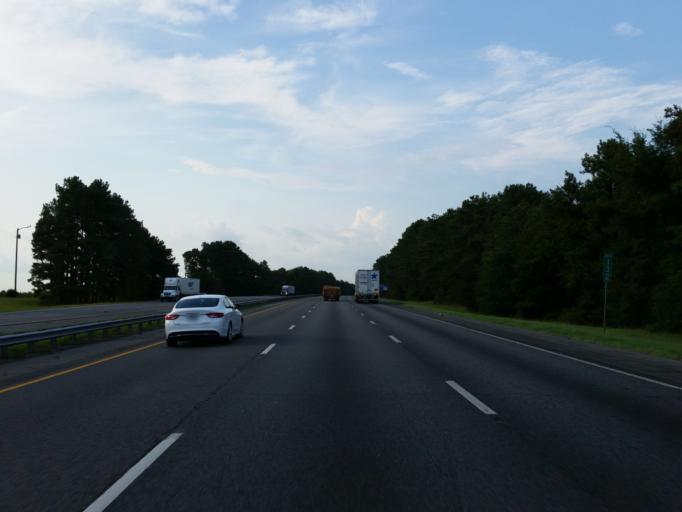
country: US
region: Georgia
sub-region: Houston County
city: Perry
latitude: 32.4100
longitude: -83.7635
